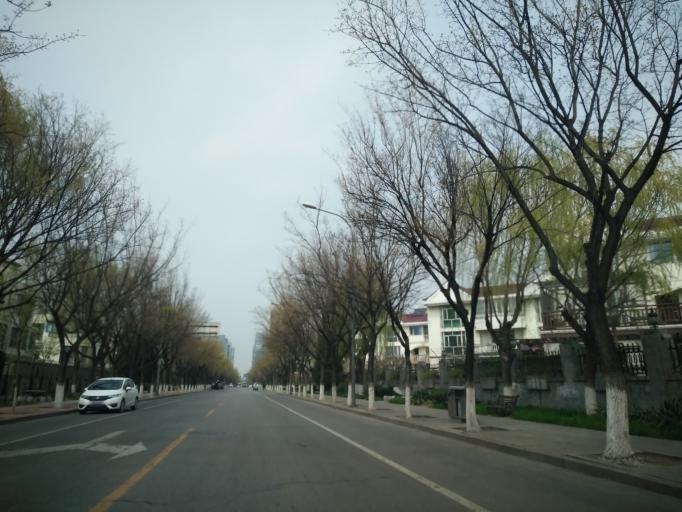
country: CN
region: Beijing
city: Jiugong
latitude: 39.7964
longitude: 116.4945
